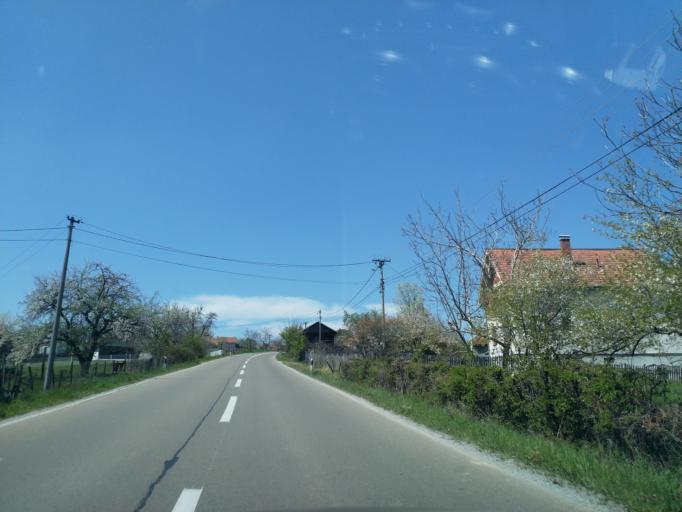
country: RS
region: Central Serbia
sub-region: Belgrade
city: Lazarevac
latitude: 44.3485
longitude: 20.3869
